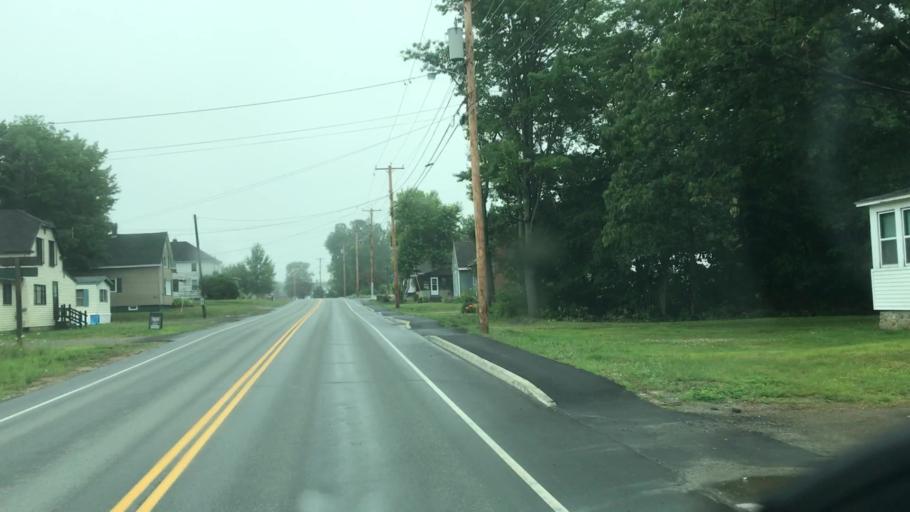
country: US
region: Maine
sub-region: Penobscot County
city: Howland
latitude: 45.2383
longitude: -68.6647
